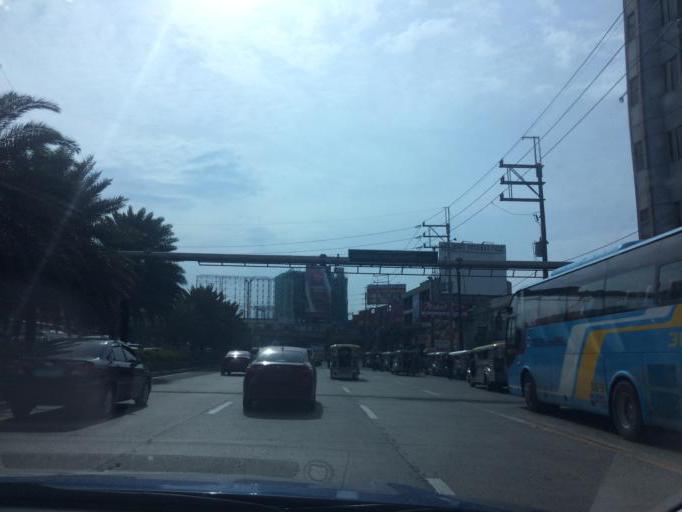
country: PH
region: Metro Manila
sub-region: Makati City
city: Makati City
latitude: 14.5375
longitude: 120.9990
